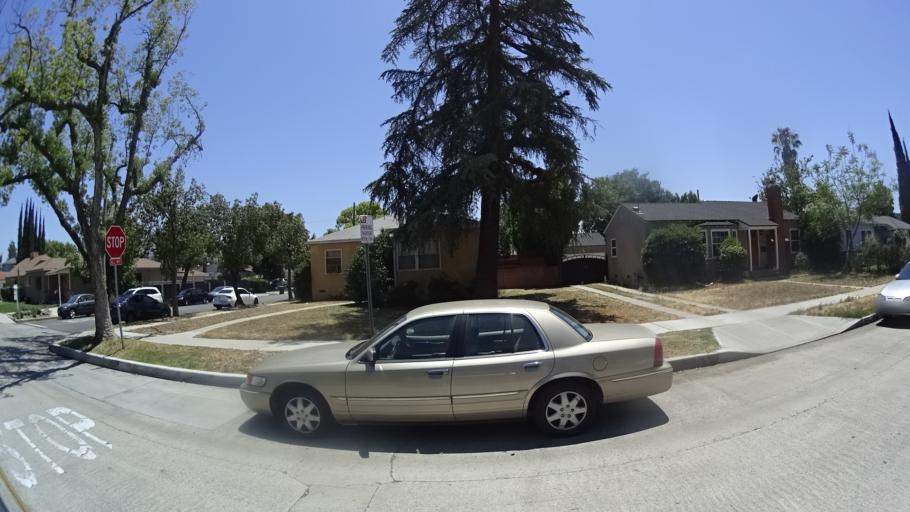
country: US
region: California
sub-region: Los Angeles County
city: North Hollywood
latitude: 34.1792
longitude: -118.3450
